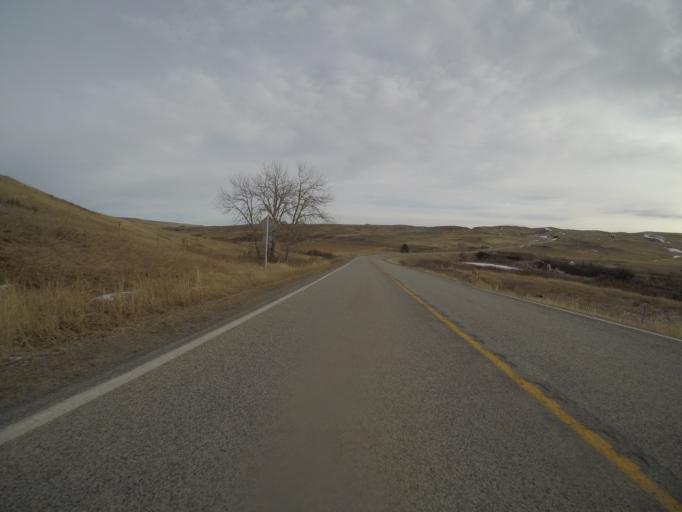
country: US
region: Montana
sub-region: Stillwater County
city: Absarokee
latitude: 45.3204
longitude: -109.4583
